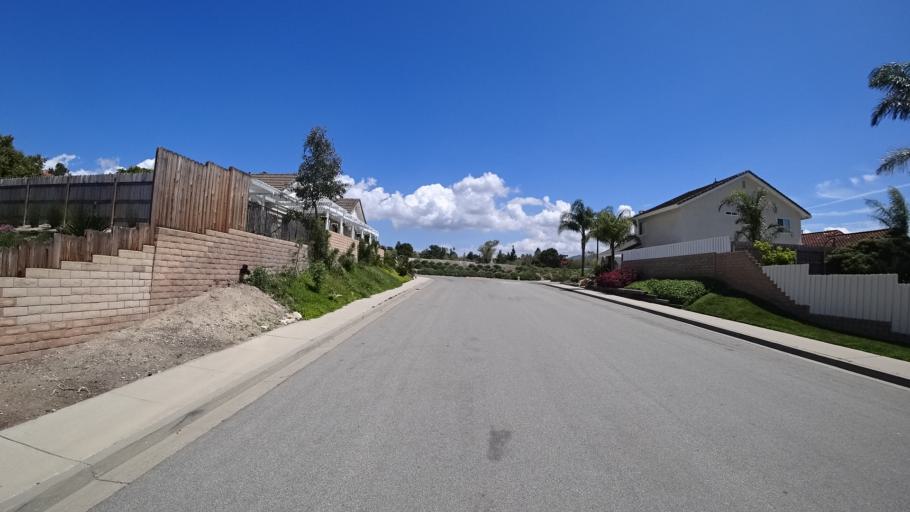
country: US
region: California
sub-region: Ventura County
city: Thousand Oaks
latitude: 34.2161
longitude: -118.8465
